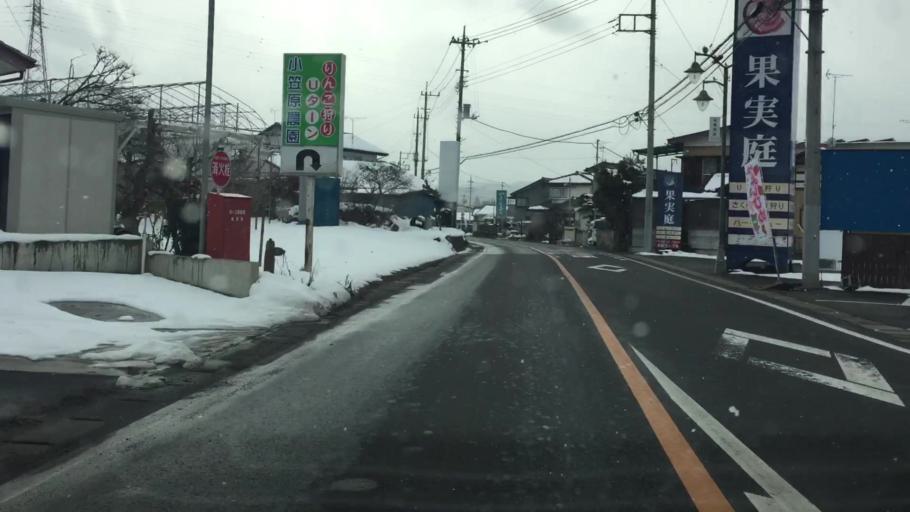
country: JP
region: Gunma
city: Numata
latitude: 36.6595
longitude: 139.0780
